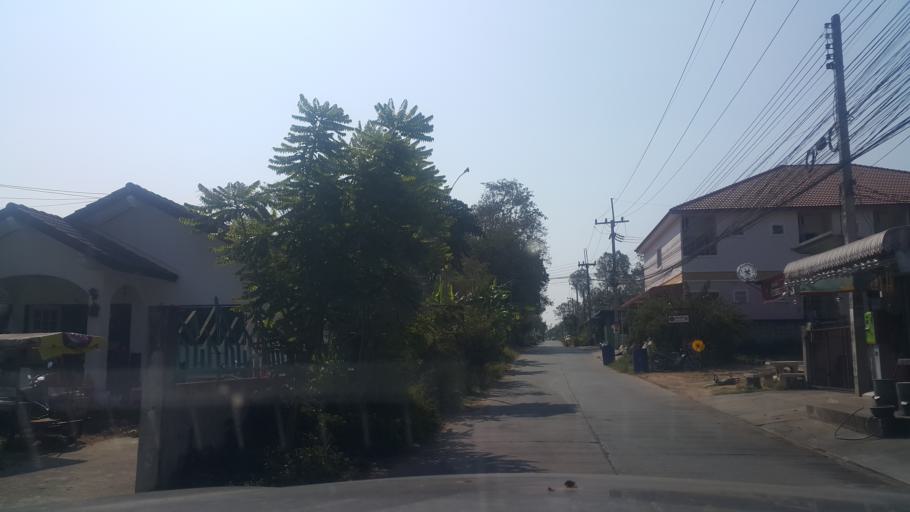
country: TH
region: Nakhon Ratchasima
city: Nakhon Ratchasima
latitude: 14.9371
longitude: 102.0360
